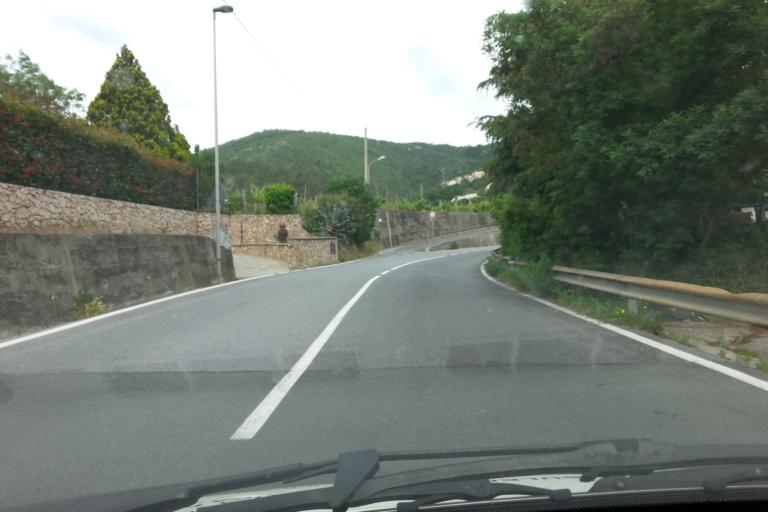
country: IT
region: Liguria
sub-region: Provincia di Savona
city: Pietra Ligure
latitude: 44.1490
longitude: 8.2680
